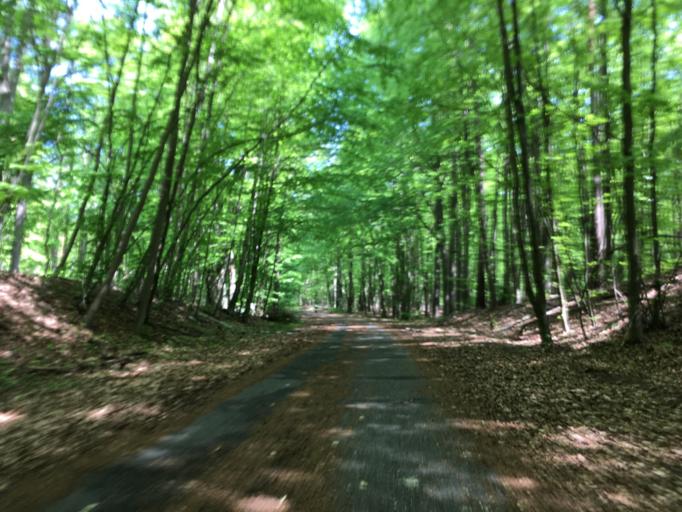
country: DE
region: Brandenburg
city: Wandlitz
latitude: 52.7322
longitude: 13.4686
